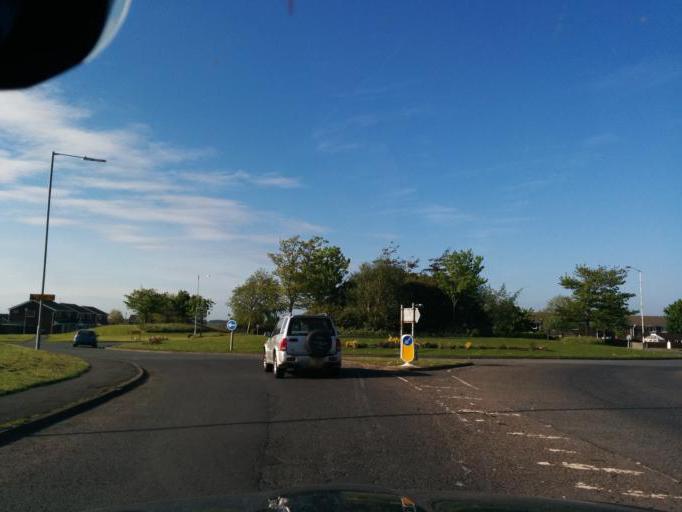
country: GB
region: England
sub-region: Northumberland
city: Cramlington
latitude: 55.0874
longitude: -1.5866
